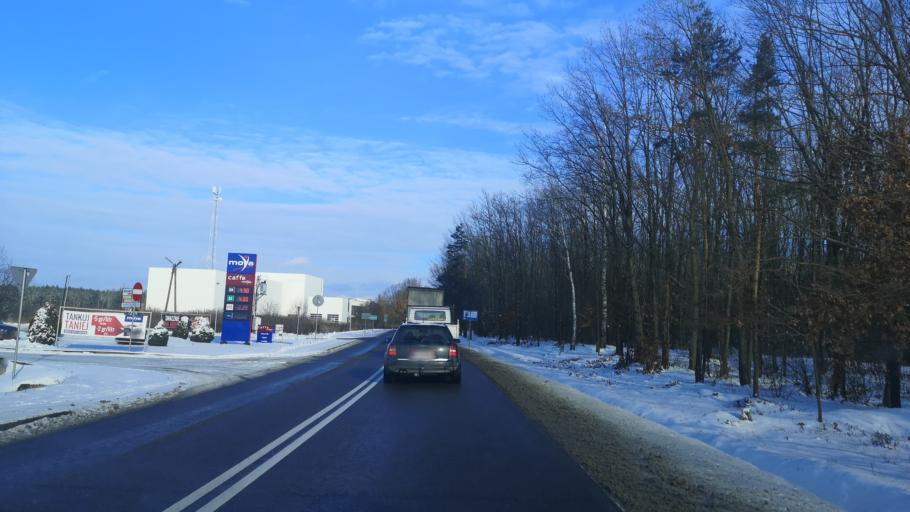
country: PL
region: Subcarpathian Voivodeship
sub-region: Powiat przeworski
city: Tryncza
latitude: 50.1444
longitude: 22.5489
